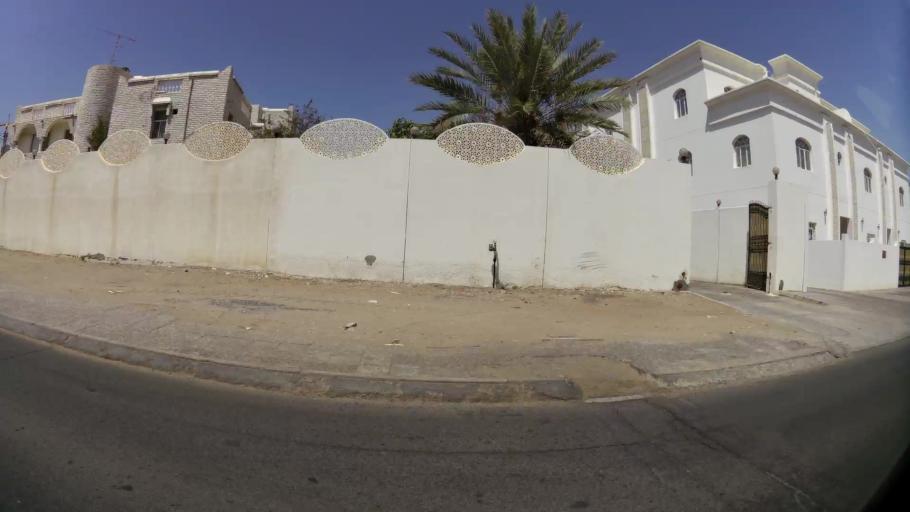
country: OM
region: Muhafazat Masqat
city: Muscat
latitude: 23.6203
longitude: 58.5035
